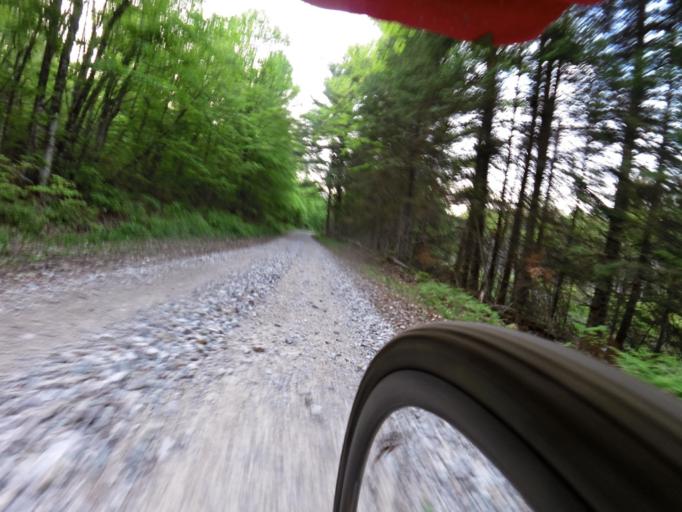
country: CA
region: Ontario
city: Arnprior
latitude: 45.1825
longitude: -76.5050
